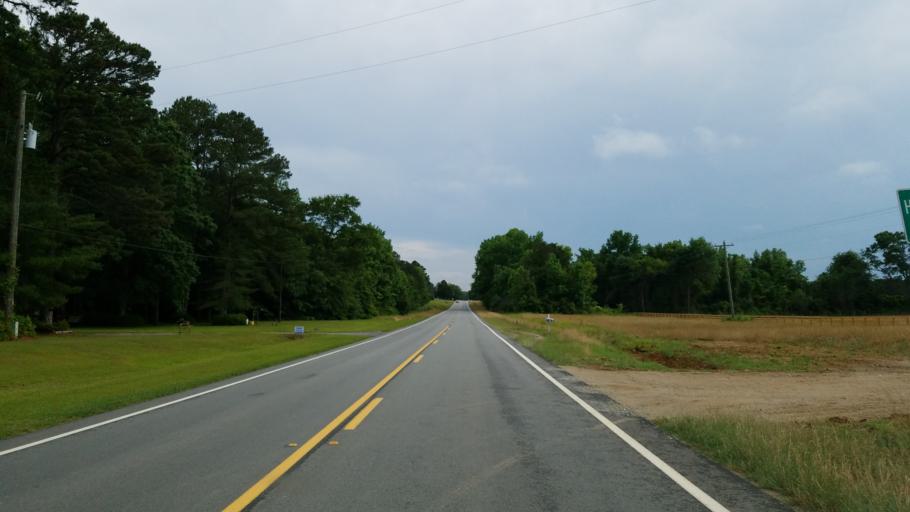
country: US
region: Georgia
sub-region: Dooly County
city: Unadilla
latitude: 32.3496
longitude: -83.7891
